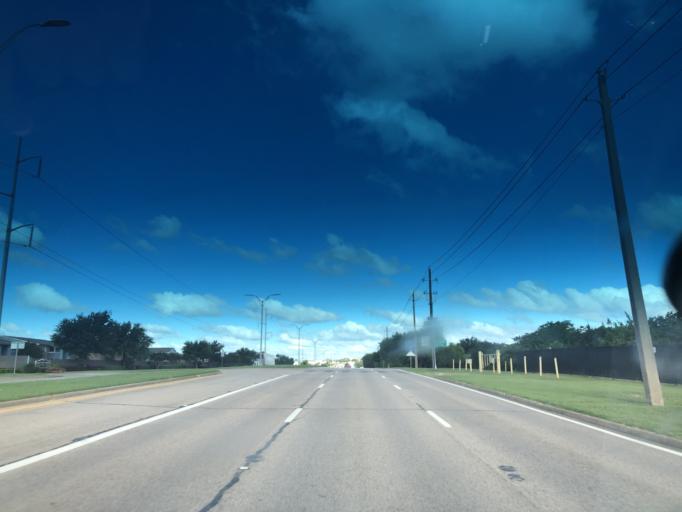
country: US
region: Texas
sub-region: Dallas County
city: Grand Prairie
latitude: 32.7112
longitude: -97.0355
